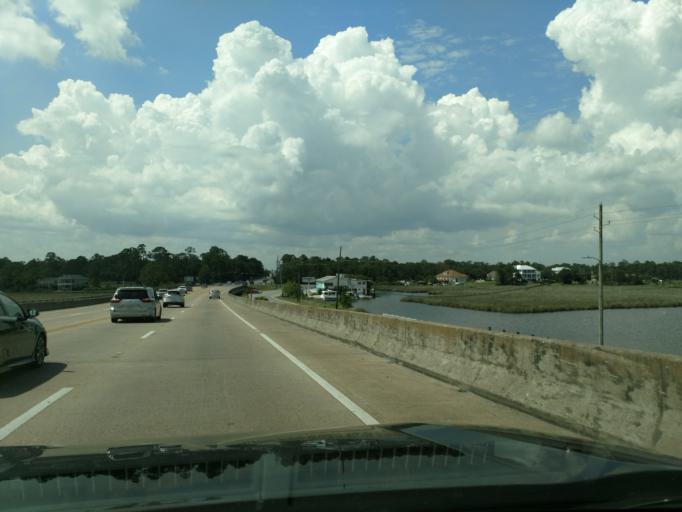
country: US
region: Mississippi
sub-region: Jackson County
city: Ocean Springs
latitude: 30.4213
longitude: -88.8285
